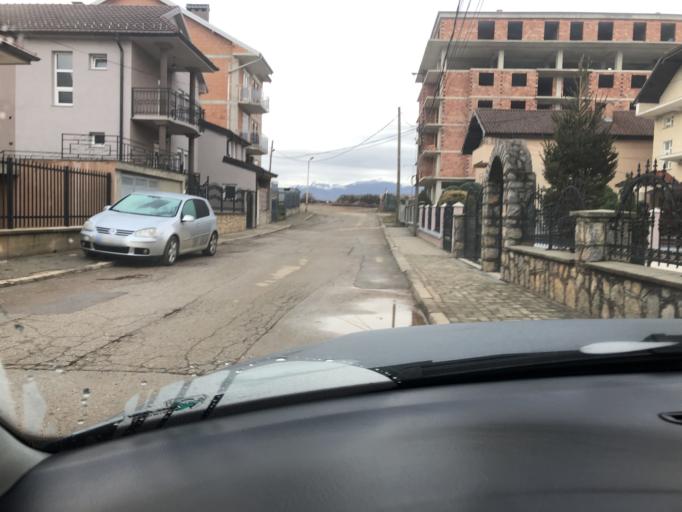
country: MK
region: Debar
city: Debar
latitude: 41.5158
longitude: 20.5273
